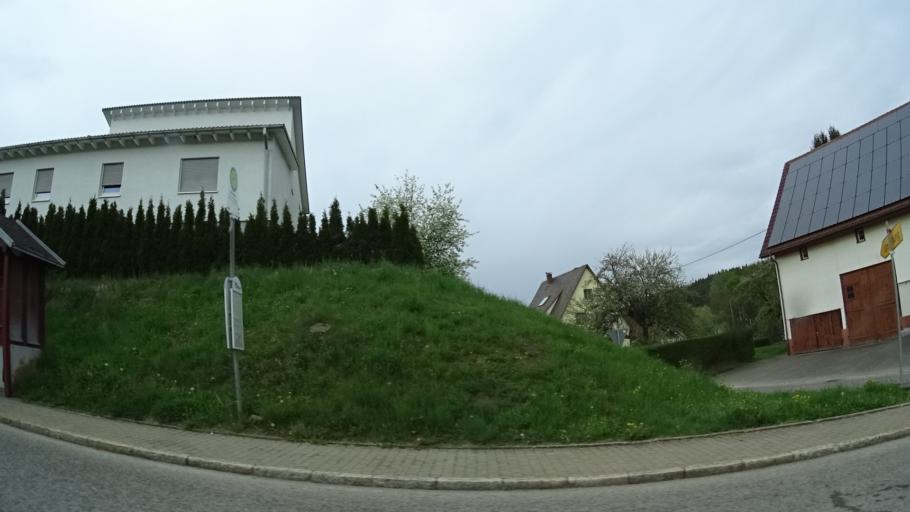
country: DE
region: Baden-Wuerttemberg
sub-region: Freiburg Region
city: Niedereschach
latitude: 48.1127
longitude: 8.4993
